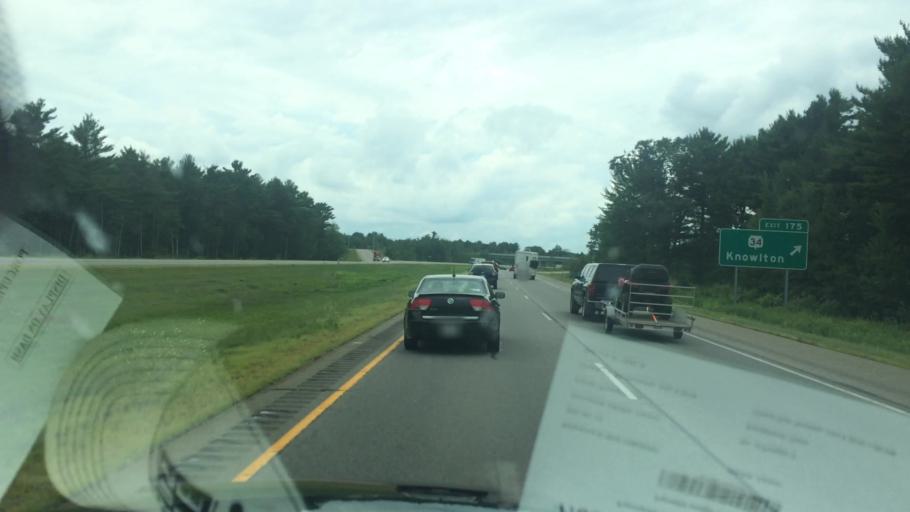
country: US
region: Wisconsin
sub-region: Marathon County
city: Mosinee
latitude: 44.7247
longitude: -89.6733
